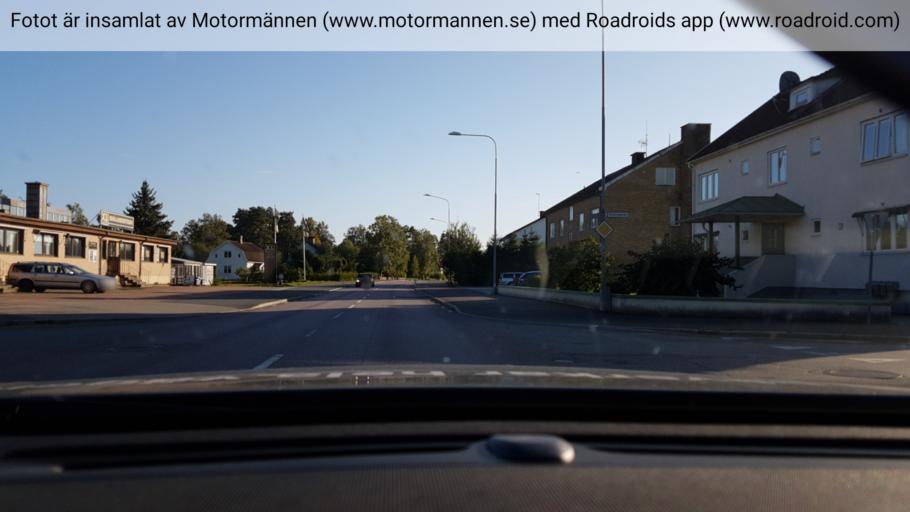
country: SE
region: Joenkoeping
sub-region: Gislaveds Kommun
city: Smalandsstenar
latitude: 57.1696
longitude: 13.4182
